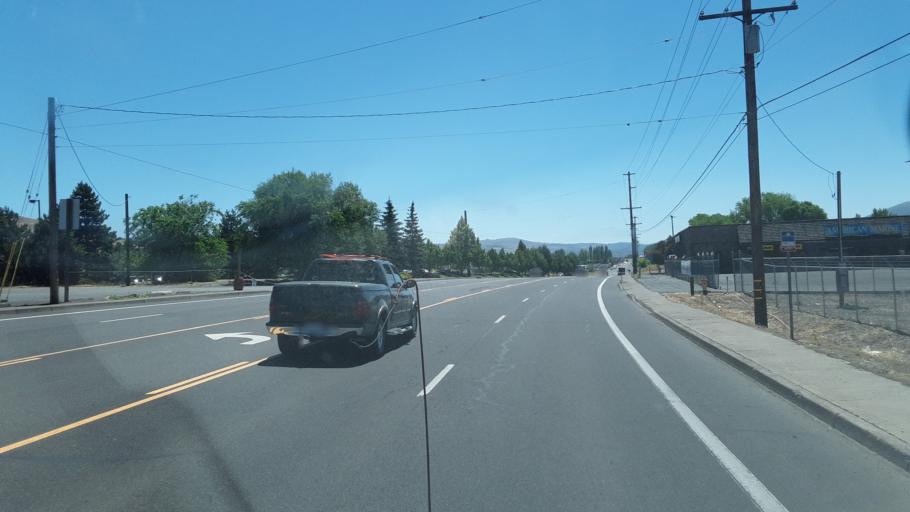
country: US
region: Oregon
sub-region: Klamath County
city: Altamont
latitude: 42.2055
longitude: -121.7118
